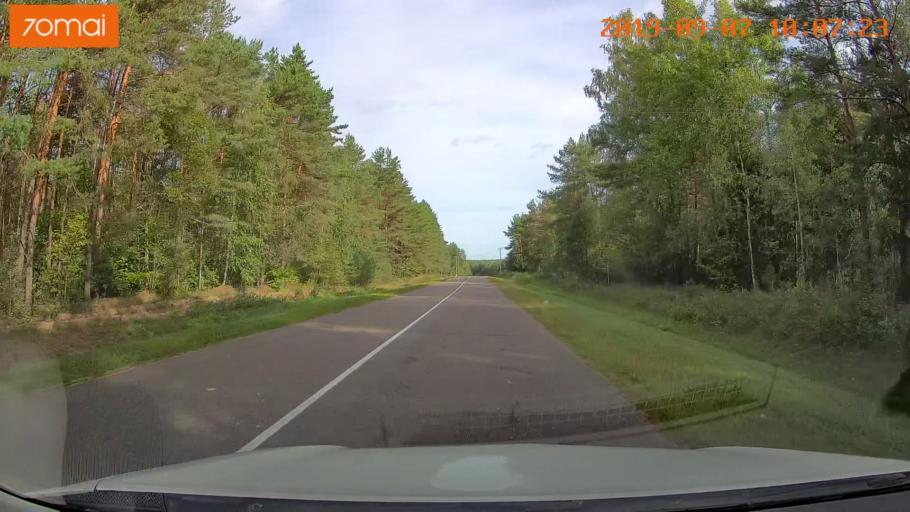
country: BY
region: Grodnenskaya
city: Voranava
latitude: 54.0749
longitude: 25.3965
